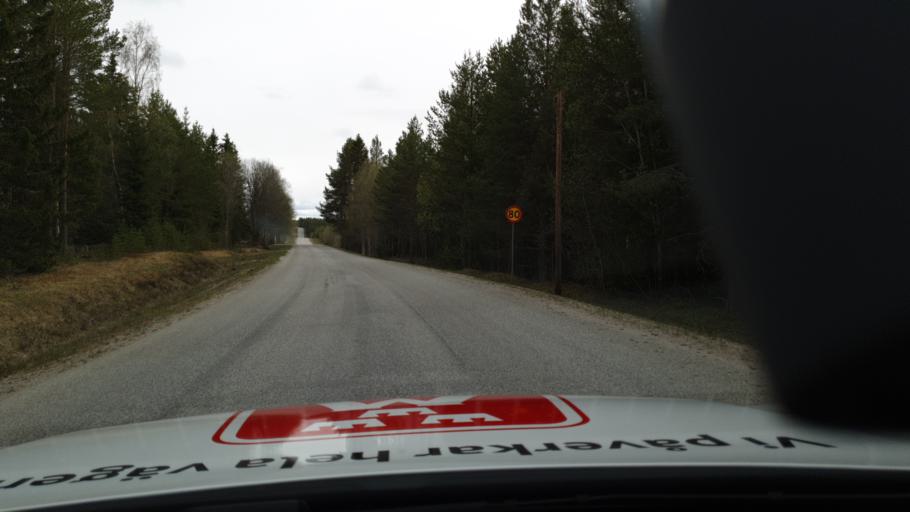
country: SE
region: Jaemtland
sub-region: OEstersunds Kommun
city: Brunflo
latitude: 62.7710
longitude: 14.9975
